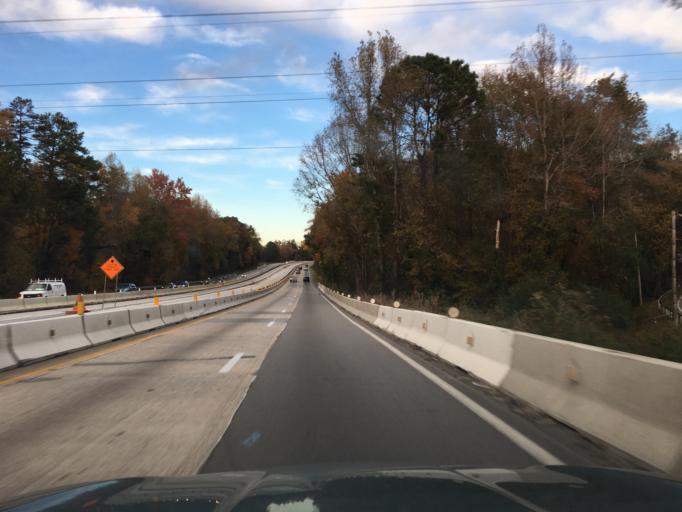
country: US
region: South Carolina
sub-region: Lexington County
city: Oak Grove
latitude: 33.9967
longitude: -81.1758
